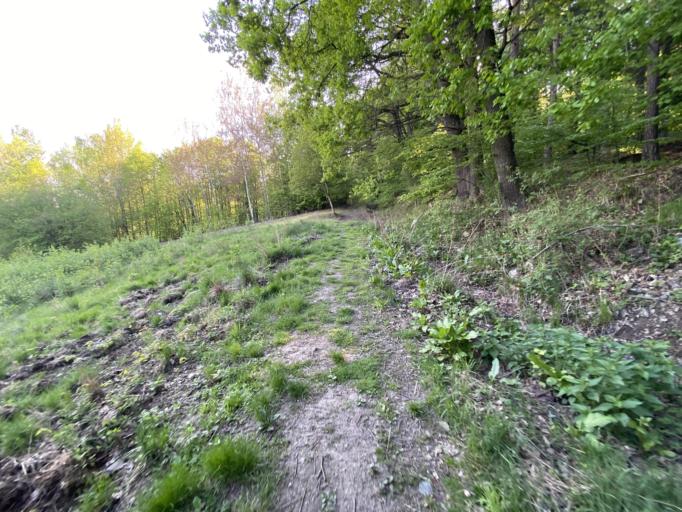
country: PL
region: Lower Silesian Voivodeship
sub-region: Powiat wroclawski
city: Sobotka
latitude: 50.8752
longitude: 16.7398
